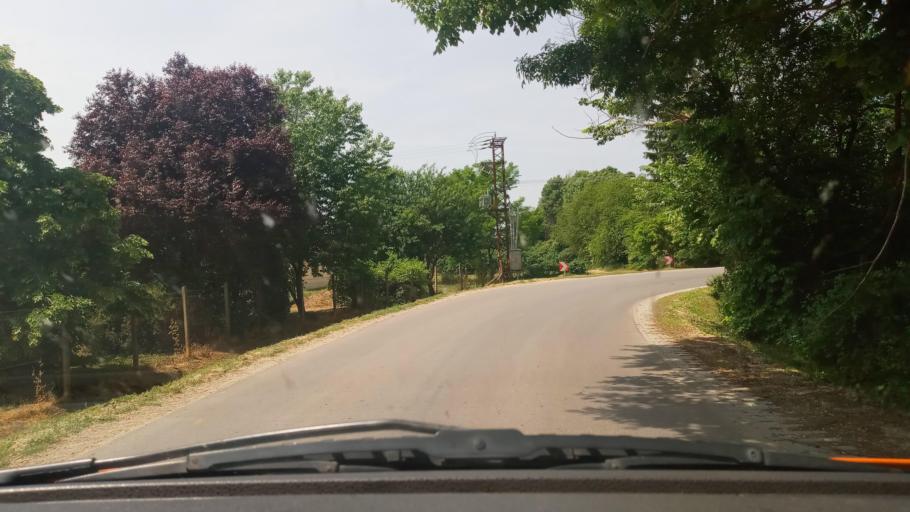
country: HU
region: Baranya
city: Szigetvar
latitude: 45.9661
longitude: 17.6832
